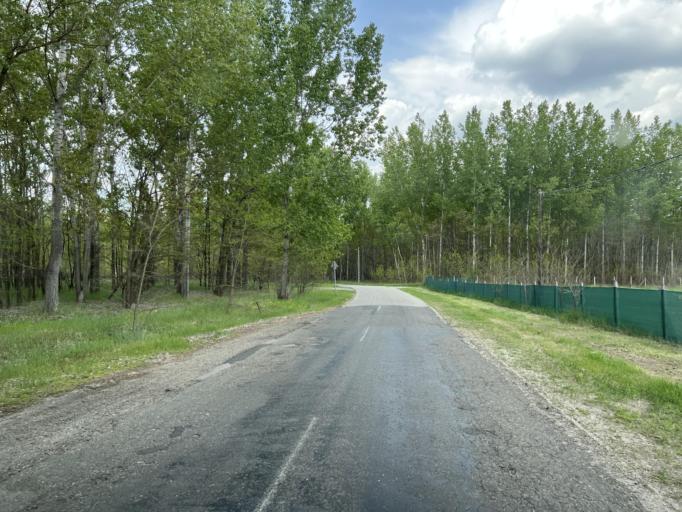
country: HU
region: Pest
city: Csemo
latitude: 47.1079
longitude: 19.7201
